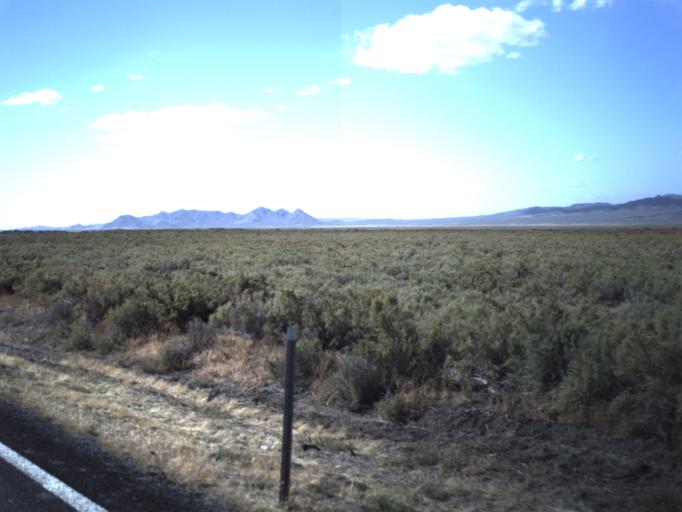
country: US
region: Utah
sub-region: Beaver County
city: Milford
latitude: 38.5615
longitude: -112.9909
